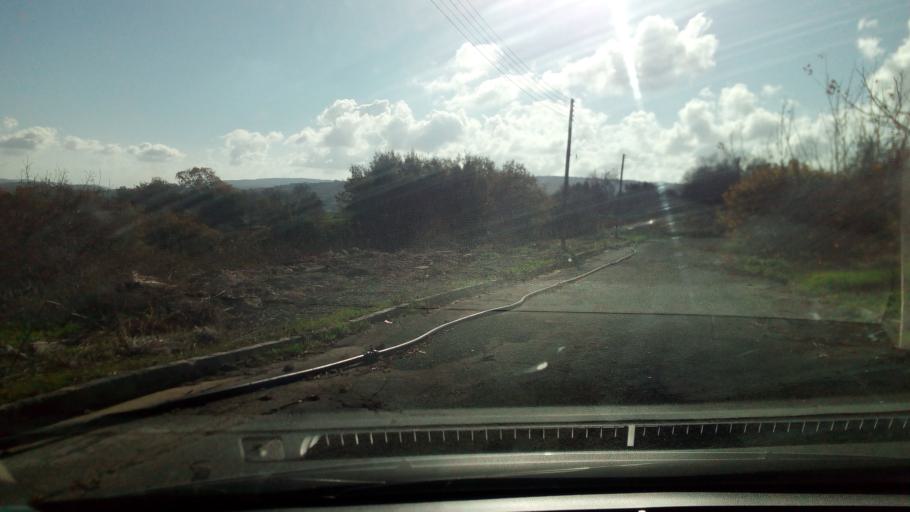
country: CY
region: Pafos
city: Mesogi
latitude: 34.8840
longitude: 32.5122
